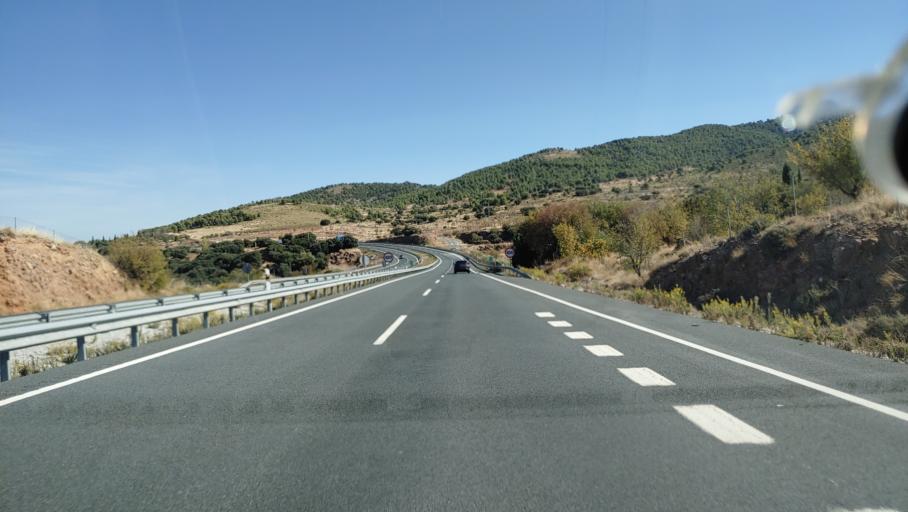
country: ES
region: Andalusia
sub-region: Provincia de Granada
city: Gor
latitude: 37.4045
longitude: -2.9235
